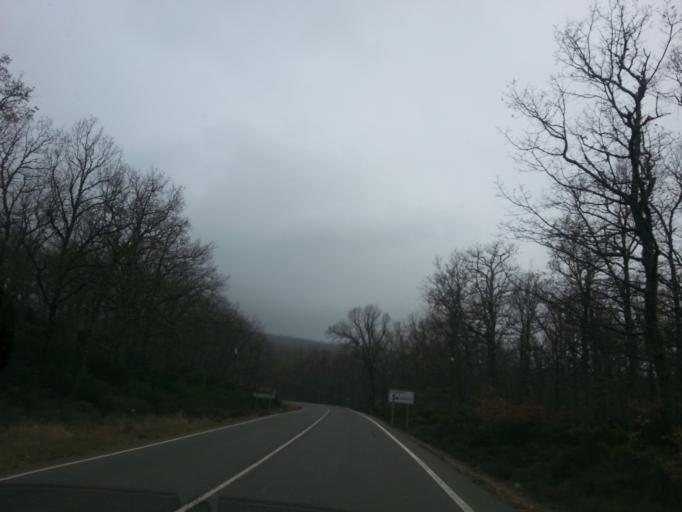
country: ES
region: Castille and Leon
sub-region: Provincia de Salamanca
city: Monforte de la Sierra
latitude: 40.4795
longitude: -6.0767
